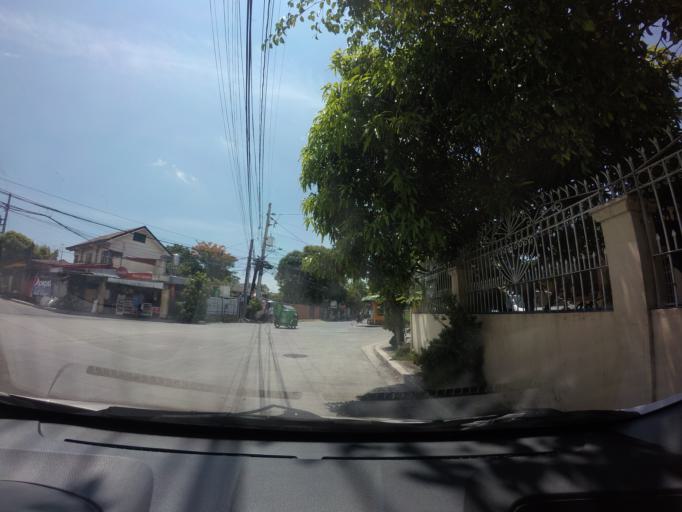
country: PH
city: Sambayanihan People's Village
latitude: 14.4232
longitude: 121.0124
